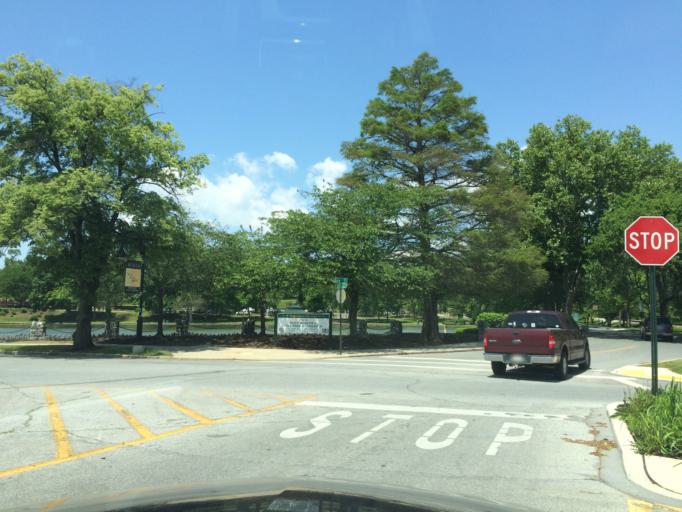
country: US
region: Maryland
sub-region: Washington County
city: Hagerstown
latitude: 39.6374
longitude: -77.7286
